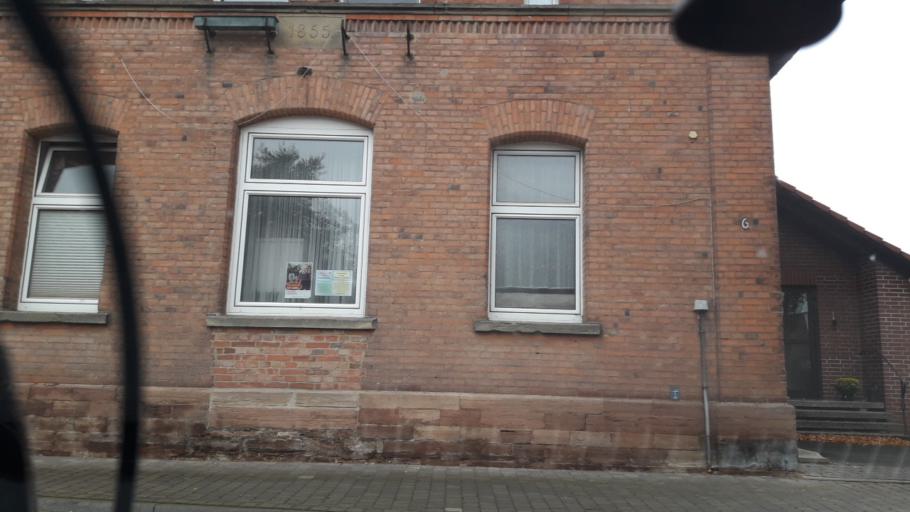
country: DE
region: Lower Saxony
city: Vienenburg
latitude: 51.9597
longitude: 10.5892
